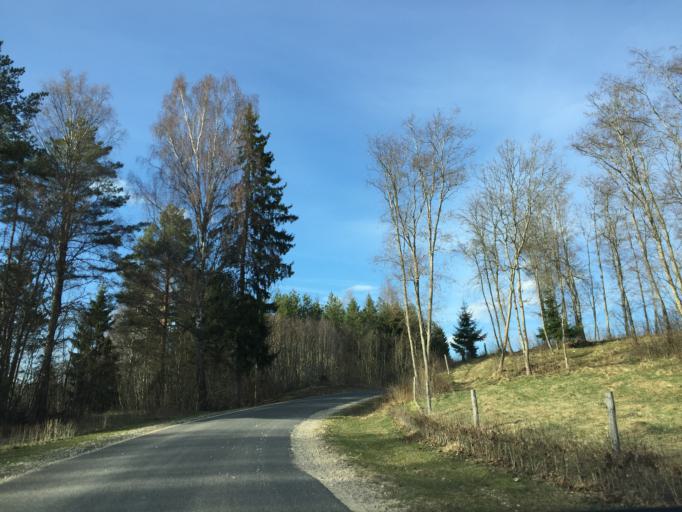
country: EE
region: Tartu
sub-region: Noo vald
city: Noo
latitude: 58.1239
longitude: 26.5742
